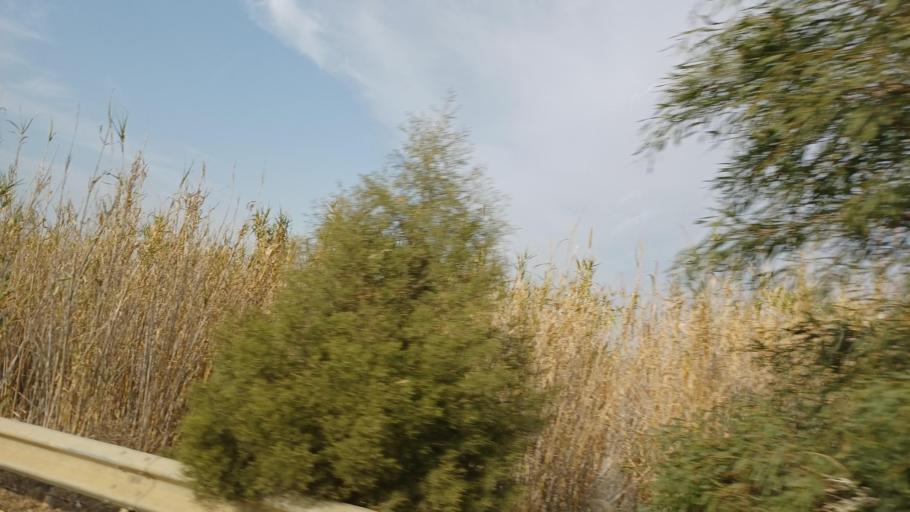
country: CY
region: Ammochostos
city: Frenaros
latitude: 35.0480
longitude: 33.9144
